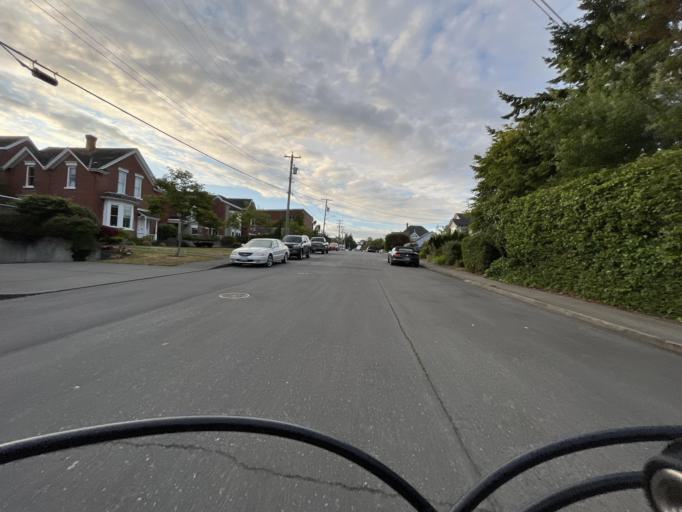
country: CA
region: British Columbia
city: Victoria
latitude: 48.4289
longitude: -123.3859
